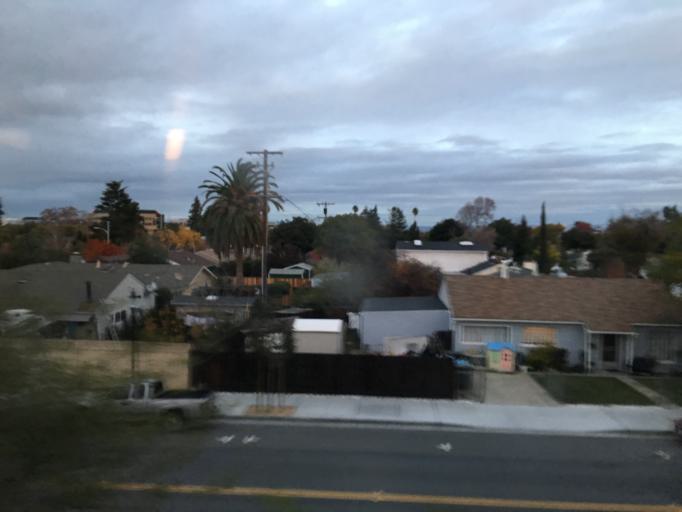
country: US
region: California
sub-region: San Mateo County
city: San Carlos
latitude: 37.5105
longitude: -122.2629
